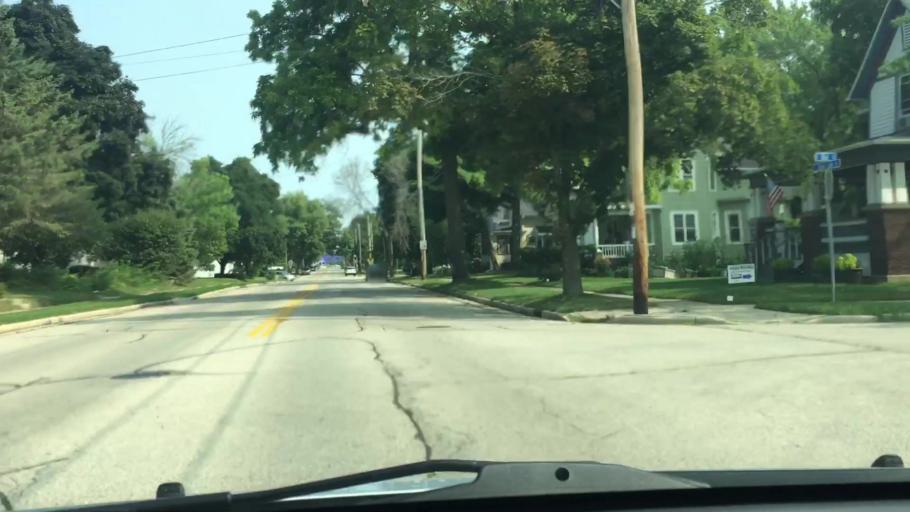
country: US
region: Wisconsin
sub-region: Waukesha County
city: Oconomowoc
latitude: 43.1037
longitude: -88.4958
